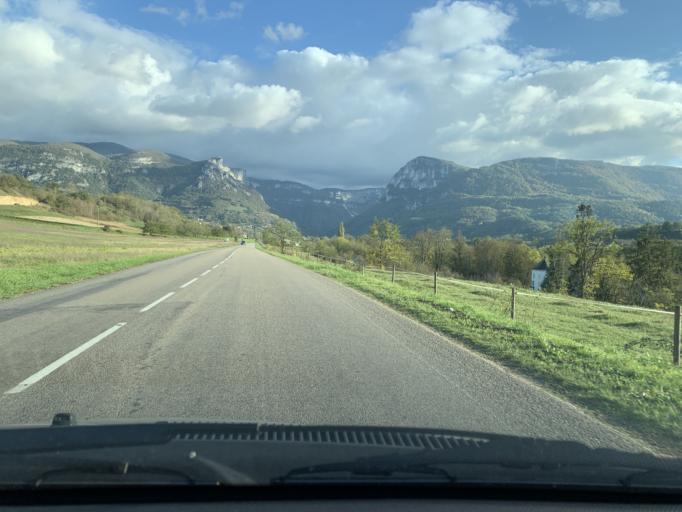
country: FR
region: Rhone-Alpes
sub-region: Departement de la Drome
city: Saint-Jean-en-Royans
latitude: 45.0381
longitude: 5.3017
